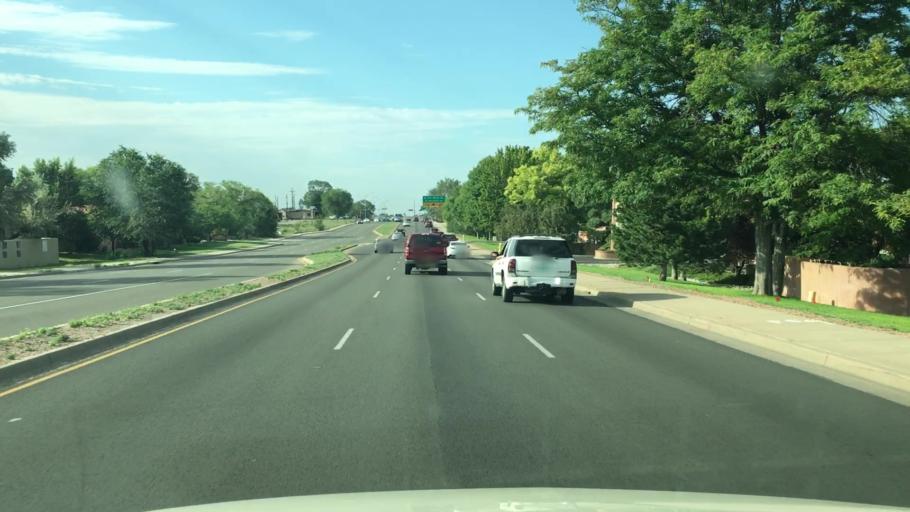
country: US
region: New Mexico
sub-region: Santa Fe County
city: Santa Fe
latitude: 35.6657
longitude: -105.9563
